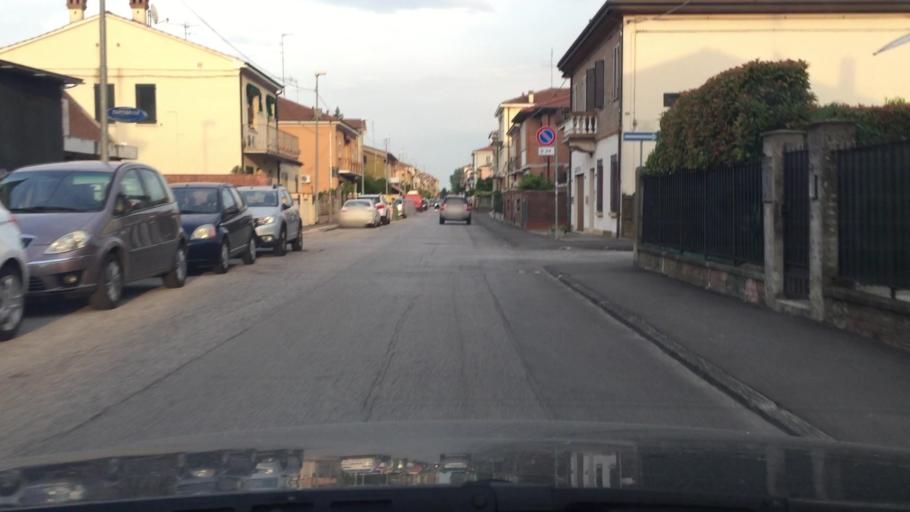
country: IT
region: Emilia-Romagna
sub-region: Provincia di Ferrara
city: Ferrara
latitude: 44.8229
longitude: 11.6089
